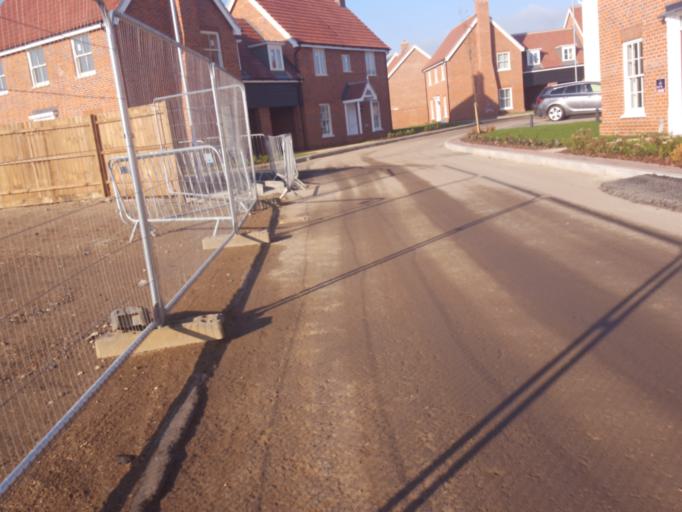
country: GB
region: England
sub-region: Essex
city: Brightlingsea
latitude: 51.8133
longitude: 1.0363
